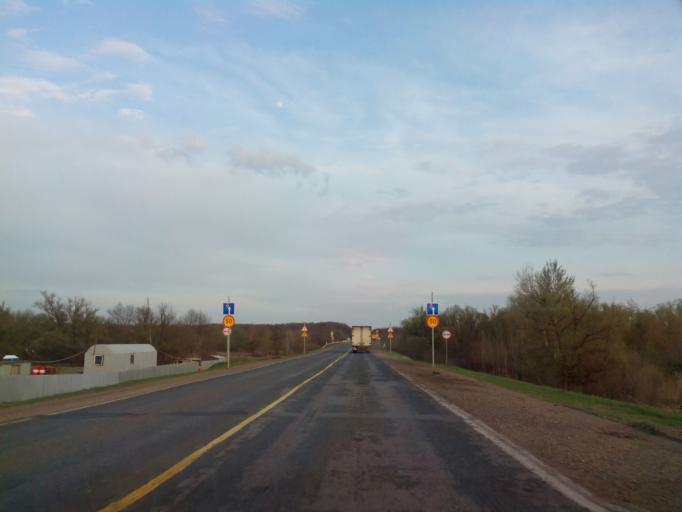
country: RU
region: Rjazan
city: Ryazhsk
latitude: 53.7160
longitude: 39.9211
